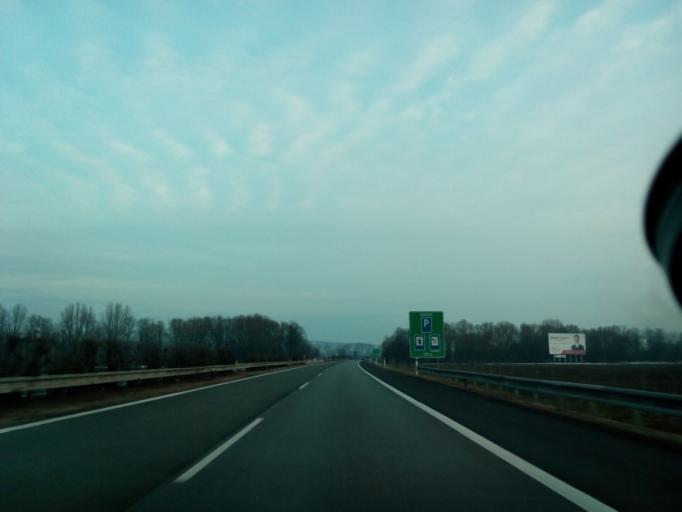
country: SK
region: Kosicky
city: Kosice
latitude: 48.8411
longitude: 21.2984
